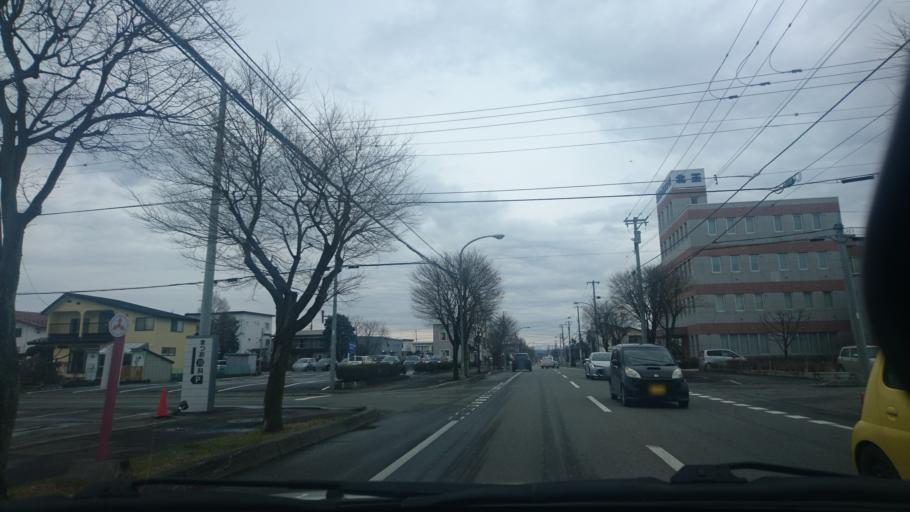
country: JP
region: Hokkaido
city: Obihiro
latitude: 42.9317
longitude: 143.1929
